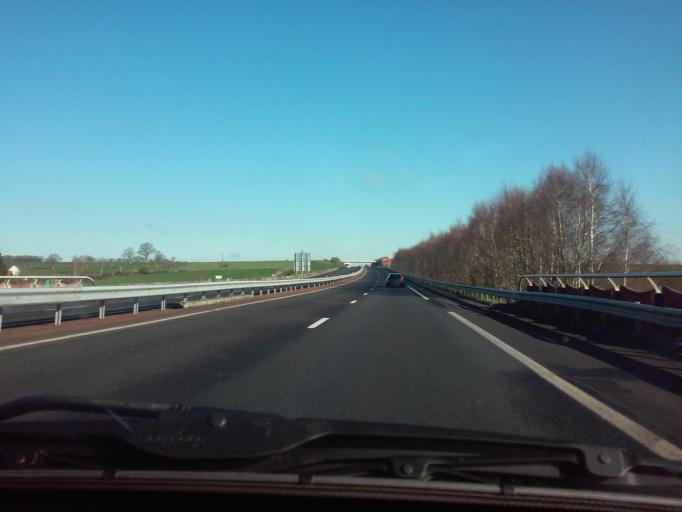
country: FR
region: Lower Normandy
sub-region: Departement de la Manche
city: Ducey
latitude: 48.5962
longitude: -1.3296
